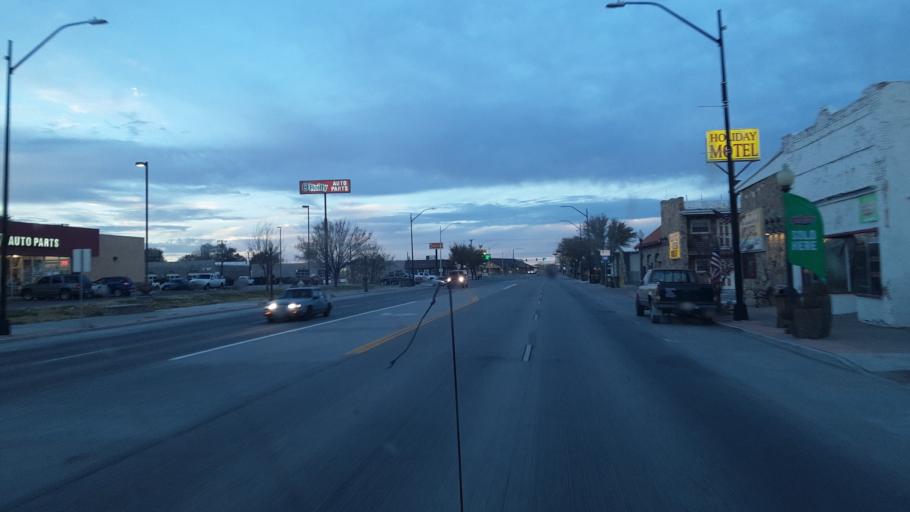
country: US
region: Colorado
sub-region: Prowers County
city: Lamar
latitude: 38.0933
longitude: -102.6195
